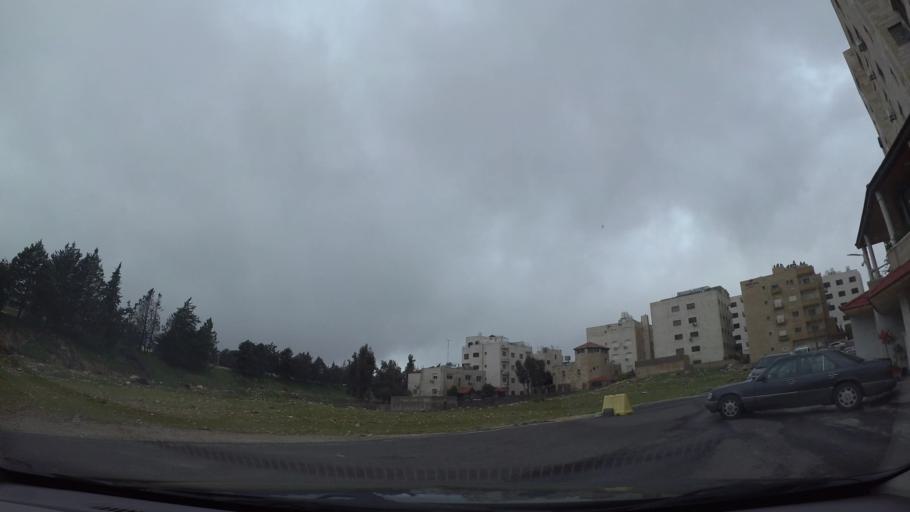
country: JO
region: Amman
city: Wadi as Sir
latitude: 31.9366
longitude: 35.8531
